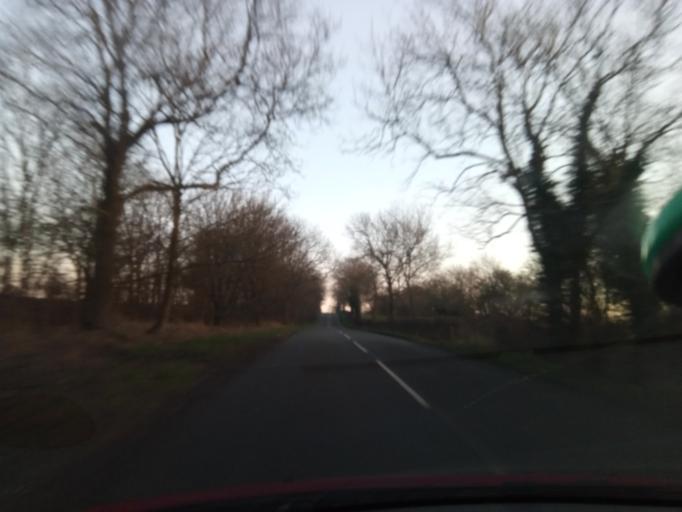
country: GB
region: England
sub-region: Leicestershire
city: Sileby
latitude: 52.7567
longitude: -1.0979
